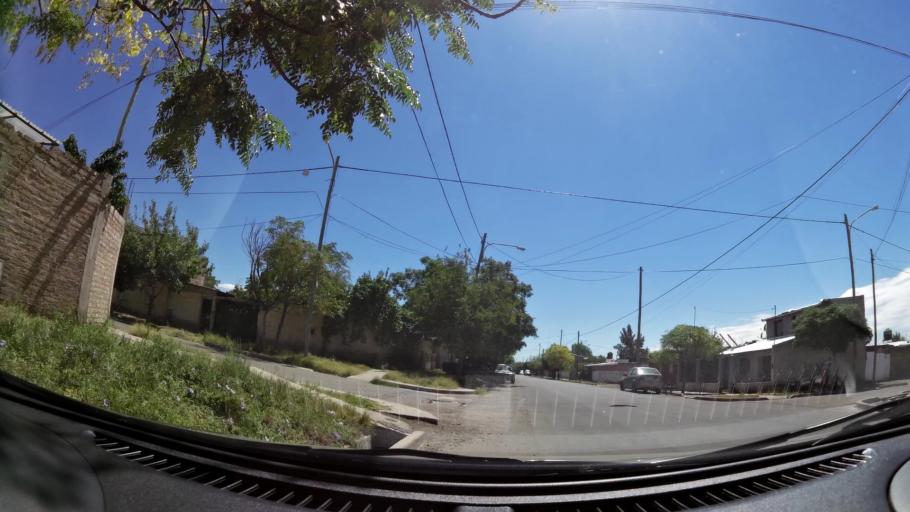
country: AR
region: Mendoza
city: Las Heras
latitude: -32.8511
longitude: -68.8713
